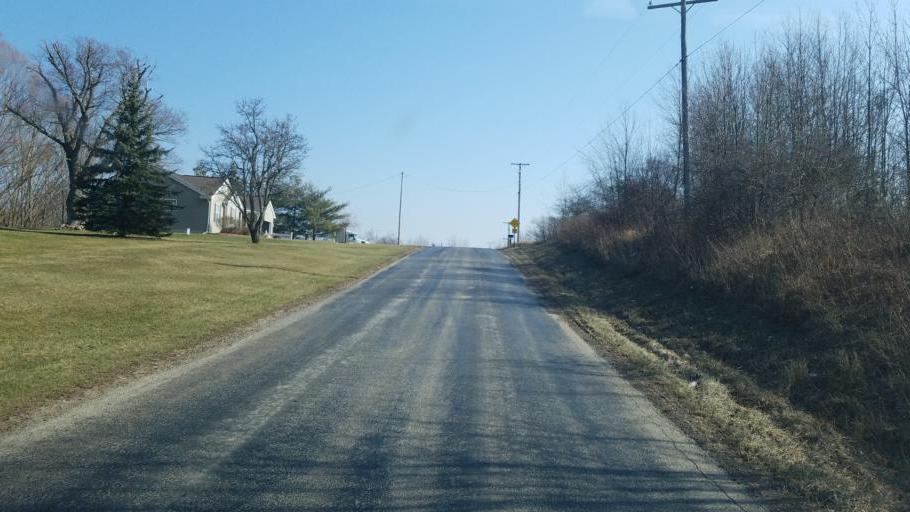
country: US
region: Ohio
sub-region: Richland County
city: Lincoln Heights
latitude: 40.8486
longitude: -82.5263
